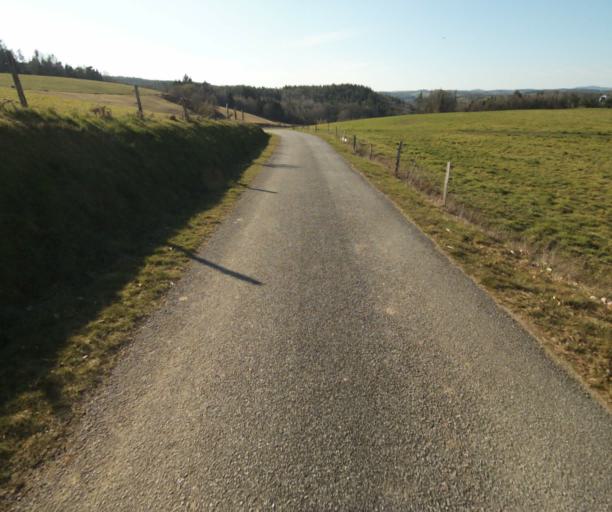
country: FR
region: Limousin
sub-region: Departement de la Correze
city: Chamboulive
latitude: 45.4871
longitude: 1.7318
